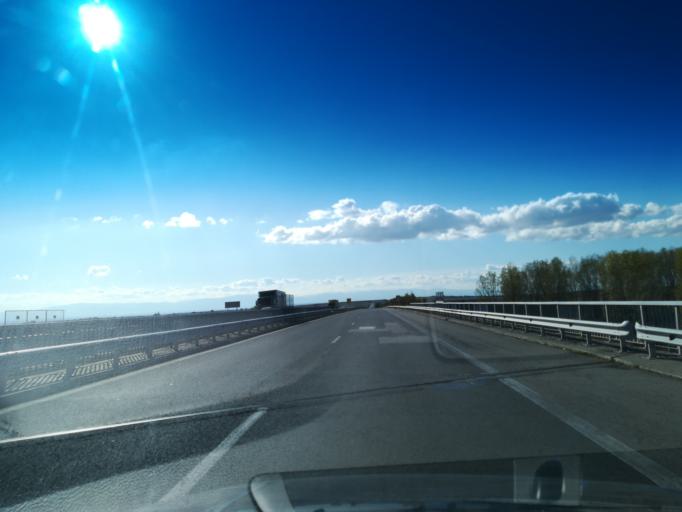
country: BG
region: Stara Zagora
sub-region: Obshtina Chirpan
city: Chirpan
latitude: 42.2188
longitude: 25.3294
